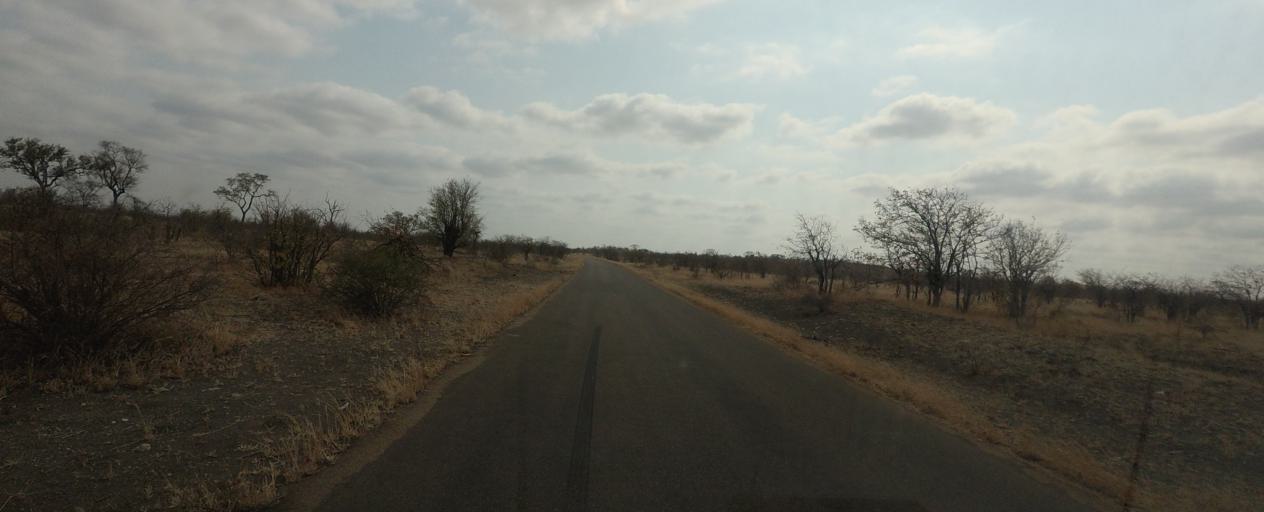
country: ZA
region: Limpopo
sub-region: Vhembe District Municipality
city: Mutale
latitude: -22.5746
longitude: 31.1886
